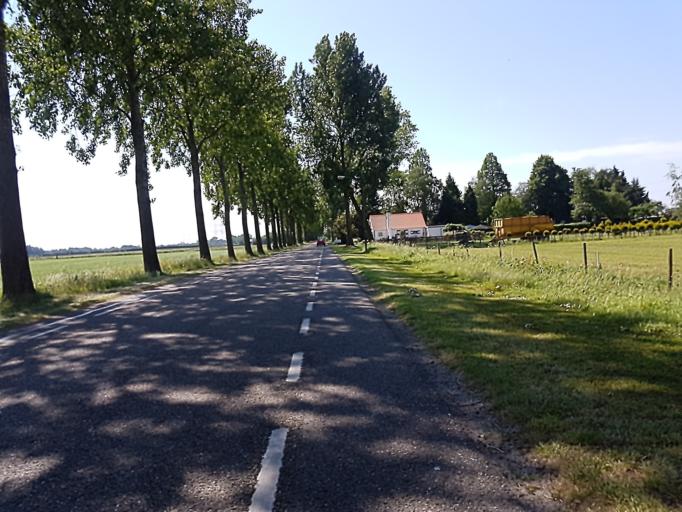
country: NL
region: North Brabant
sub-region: Gemeente Dongen
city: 's Gravenmoer
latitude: 51.6601
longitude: 4.9886
